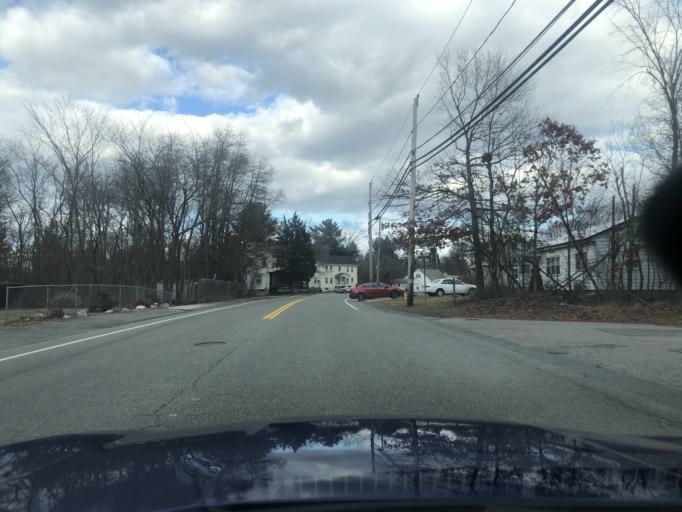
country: US
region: Massachusetts
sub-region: Plymouth County
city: Brockton
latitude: 42.1030
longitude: -71.0067
